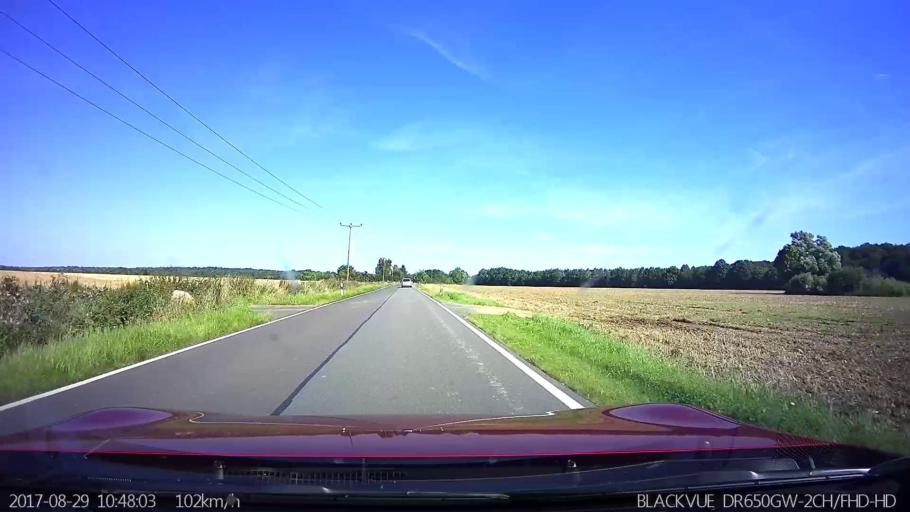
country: DE
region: Mecklenburg-Vorpommern
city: Velgast
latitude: 54.2347
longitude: 12.8253
